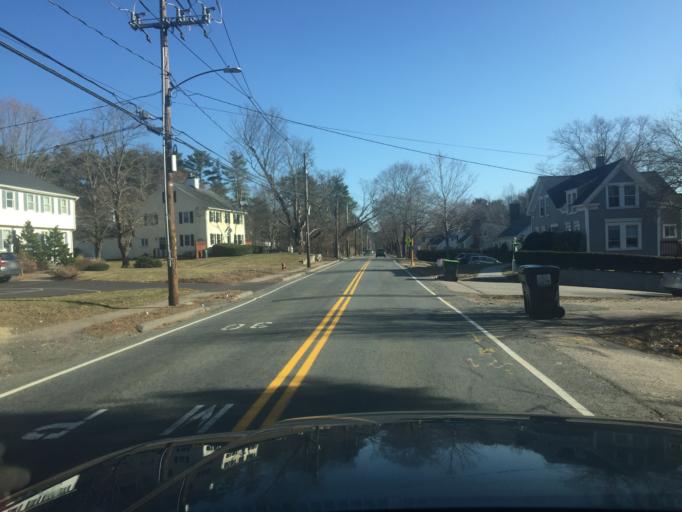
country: US
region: Massachusetts
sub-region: Norfolk County
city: Millis-Clicquot
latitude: 42.1632
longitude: -71.3548
